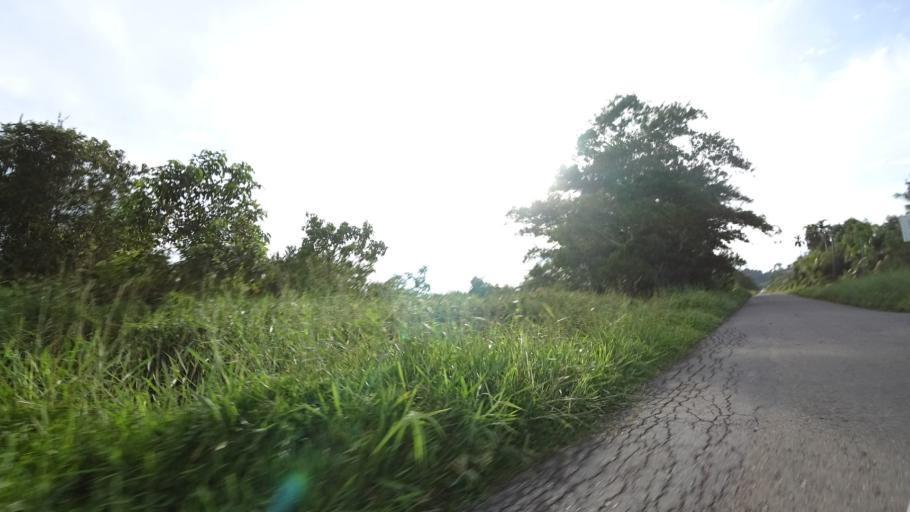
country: BN
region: Brunei and Muara
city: Bandar Seri Begawan
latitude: 4.8165
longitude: 114.8246
